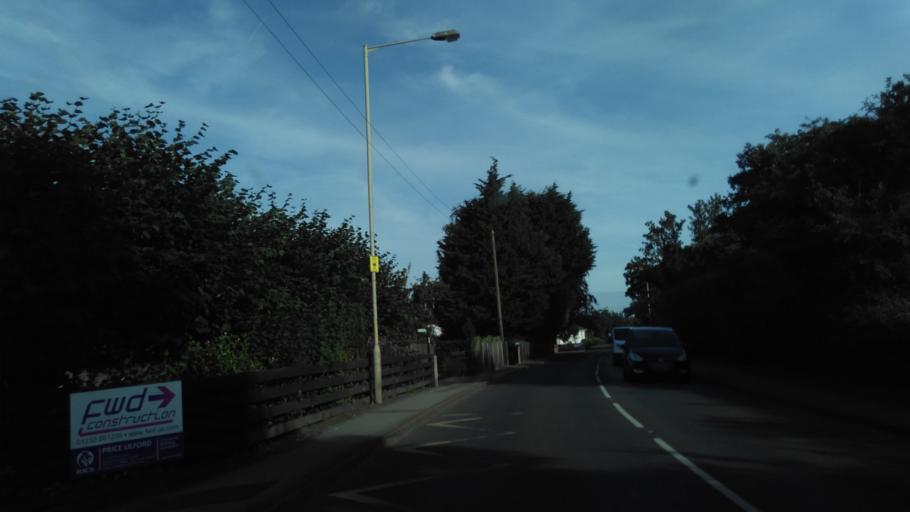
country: GB
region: England
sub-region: Kent
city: Blean
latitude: 51.2942
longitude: 1.0549
